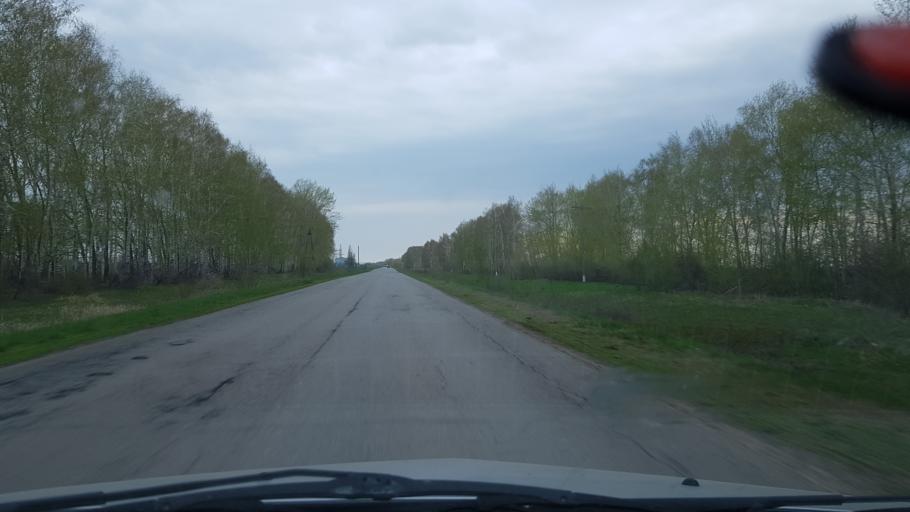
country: RU
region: Samara
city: Podstepki
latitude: 53.6654
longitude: 49.1702
